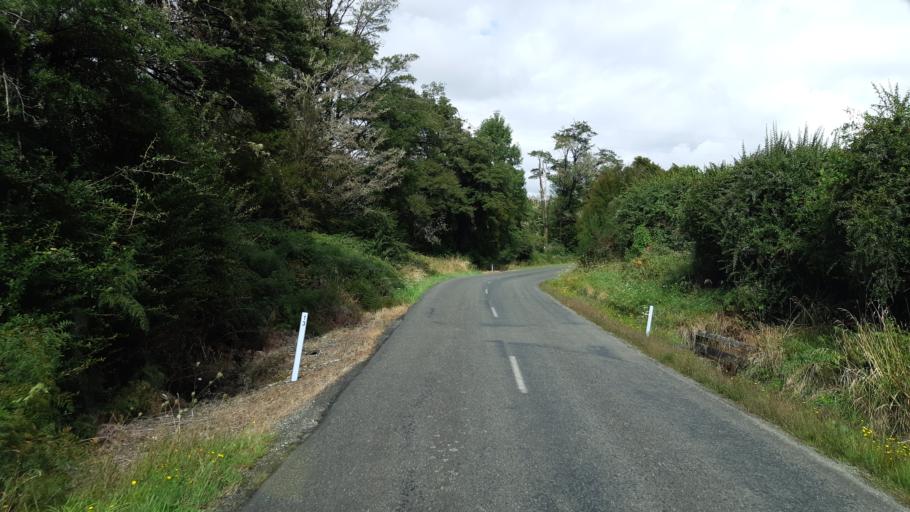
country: NZ
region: West Coast
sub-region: Buller District
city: Westport
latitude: -41.7883
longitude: 172.3665
